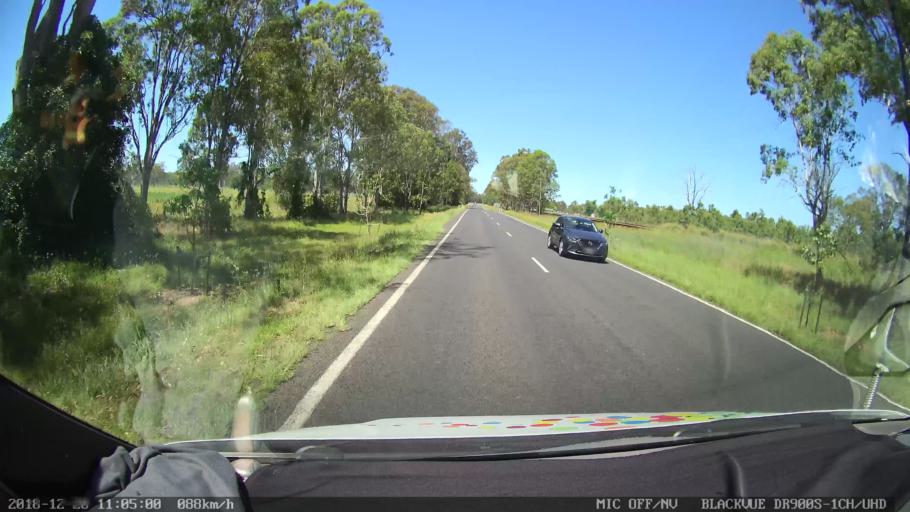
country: AU
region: New South Wales
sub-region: Richmond Valley
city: Casino
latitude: -28.8917
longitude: 153.0447
